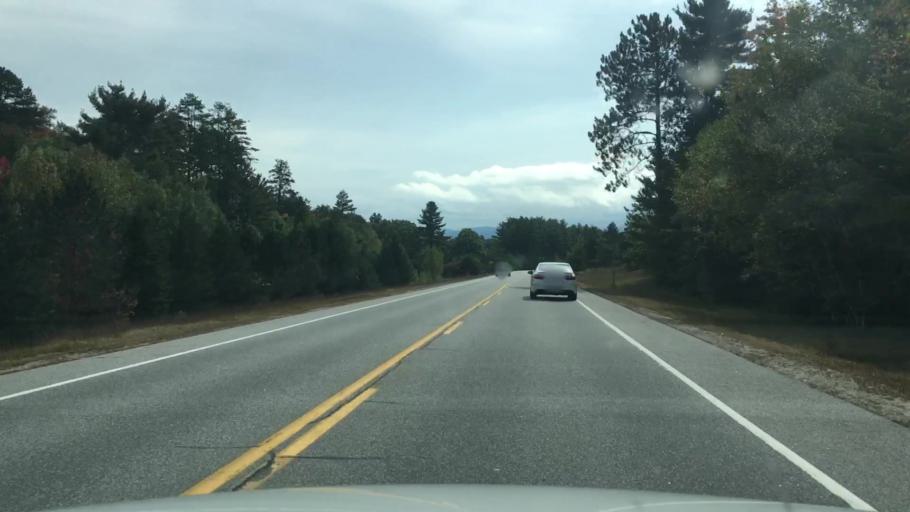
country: US
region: New Hampshire
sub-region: Carroll County
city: North Conway
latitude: 44.0271
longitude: -71.1111
